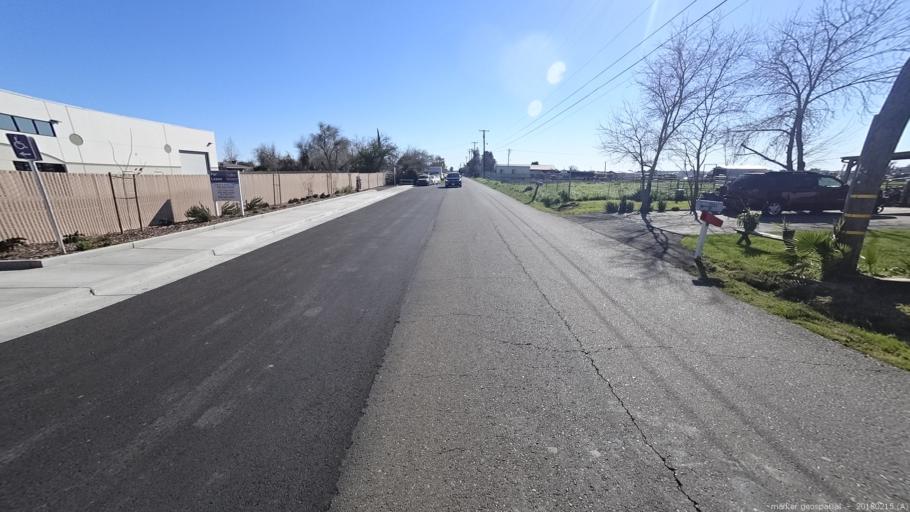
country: US
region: California
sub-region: Sacramento County
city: North Highlands
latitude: 38.6954
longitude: -121.3968
